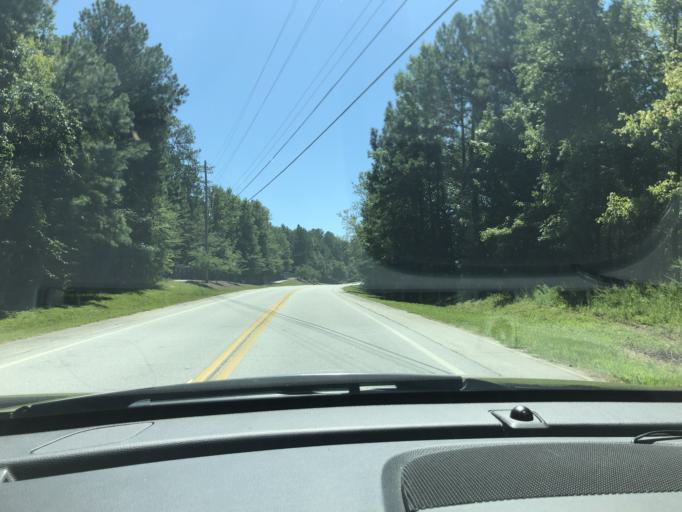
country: US
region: Georgia
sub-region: Gwinnett County
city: Grayson
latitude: 33.9111
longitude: -83.8925
